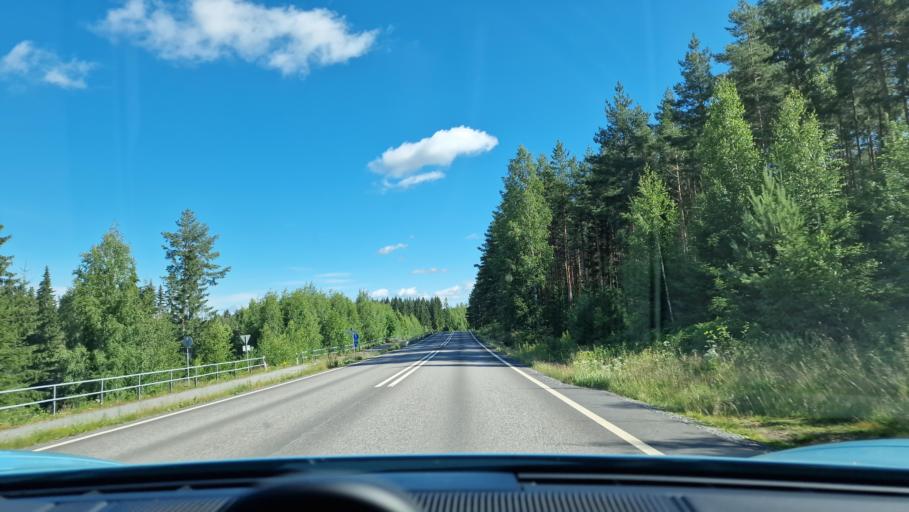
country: FI
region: Pirkanmaa
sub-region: Tampere
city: Kangasala
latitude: 61.4678
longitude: 24.1280
